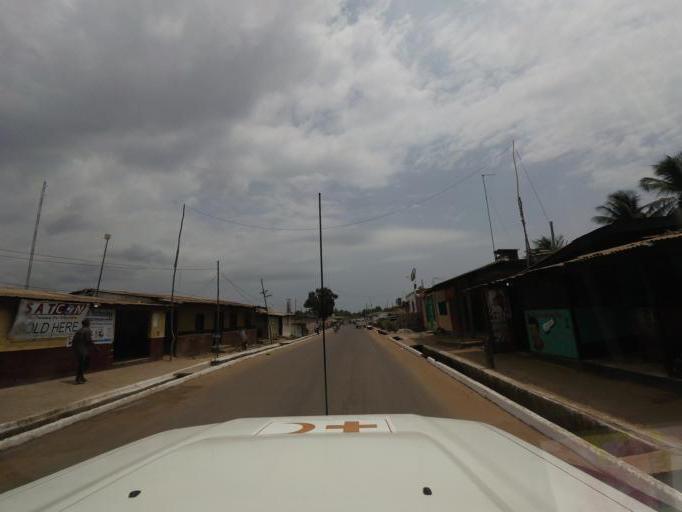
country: LR
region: Montserrado
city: Monrovia
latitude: 6.2980
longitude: -10.6841
